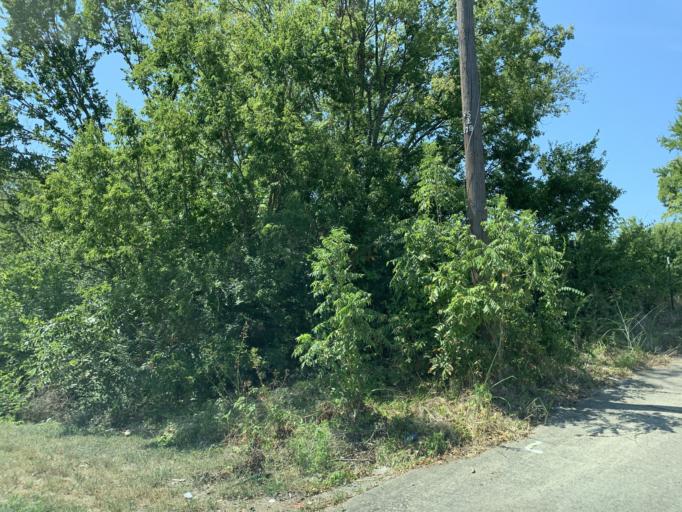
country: US
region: Texas
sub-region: Dallas County
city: Hutchins
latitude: 32.6745
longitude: -96.7479
